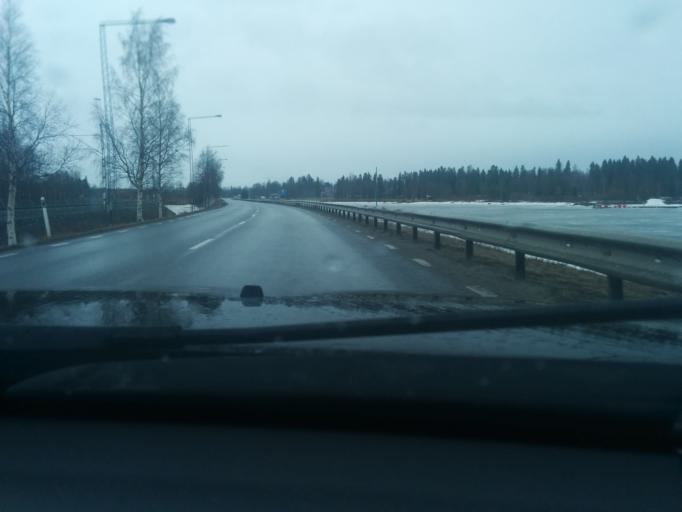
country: SE
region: Vaesterbotten
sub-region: Umea Kommun
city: Holmsund
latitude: 63.6956
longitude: 20.3560
